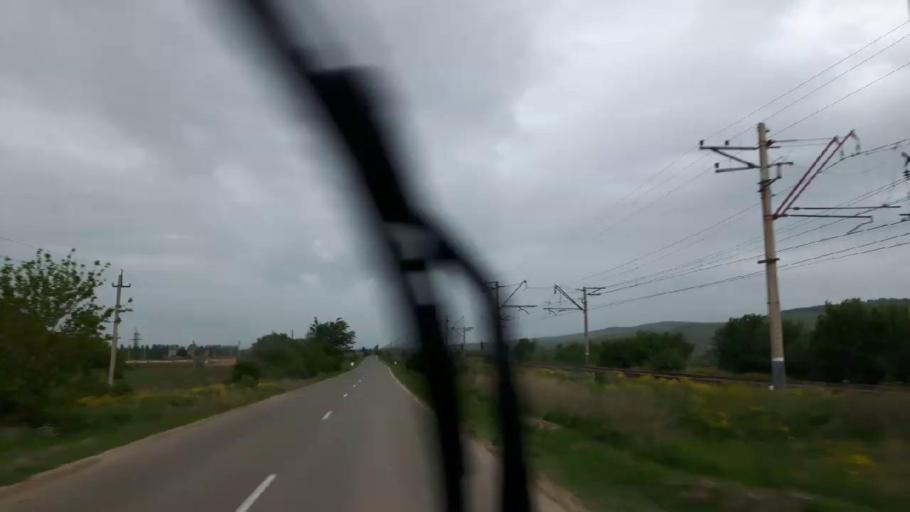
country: GE
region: Shida Kartli
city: Gori
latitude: 41.9958
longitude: 44.0234
